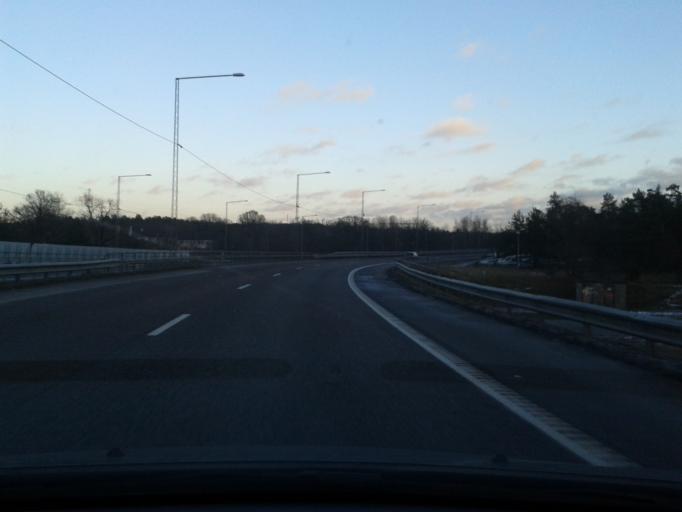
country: SE
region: Stockholm
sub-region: Nacka Kommun
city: Alta
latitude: 59.2642
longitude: 18.1422
